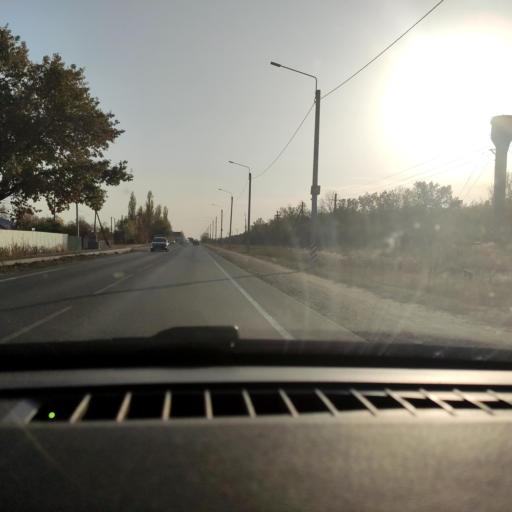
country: RU
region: Voronezj
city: Semiluki
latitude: 51.7318
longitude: 39.0400
